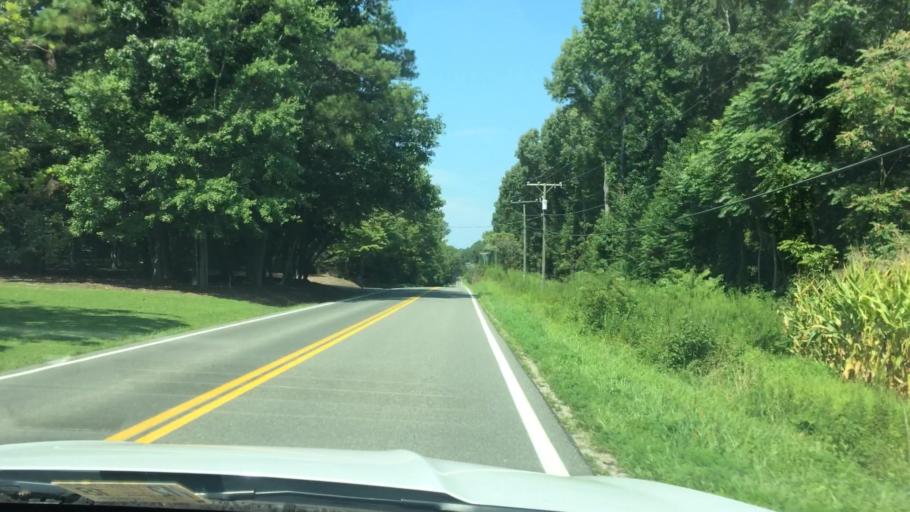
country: US
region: Virginia
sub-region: New Kent County
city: New Kent
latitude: 37.5256
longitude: -77.0148
